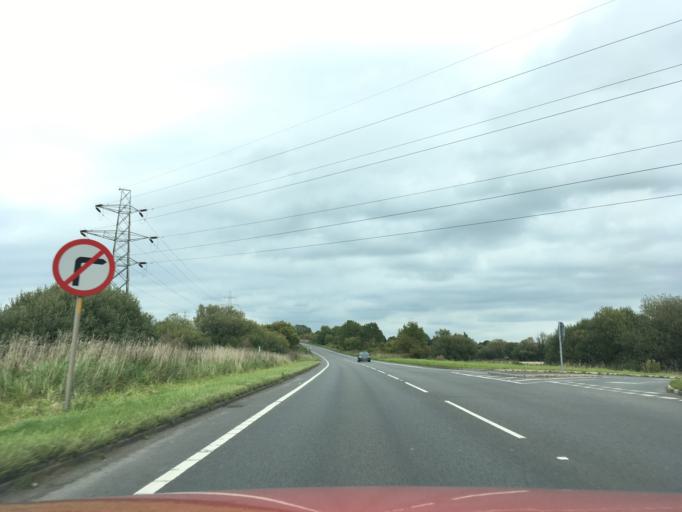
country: GB
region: Wales
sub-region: Monmouthshire
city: Magor
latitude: 51.5756
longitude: -2.8486
